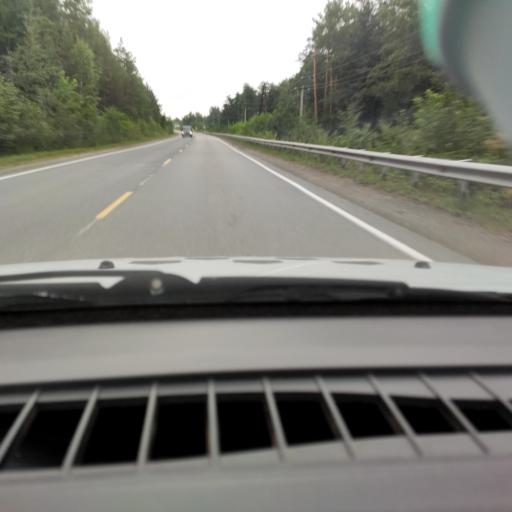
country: RU
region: Chelyabinsk
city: Kyshtym
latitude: 55.7060
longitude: 60.5063
